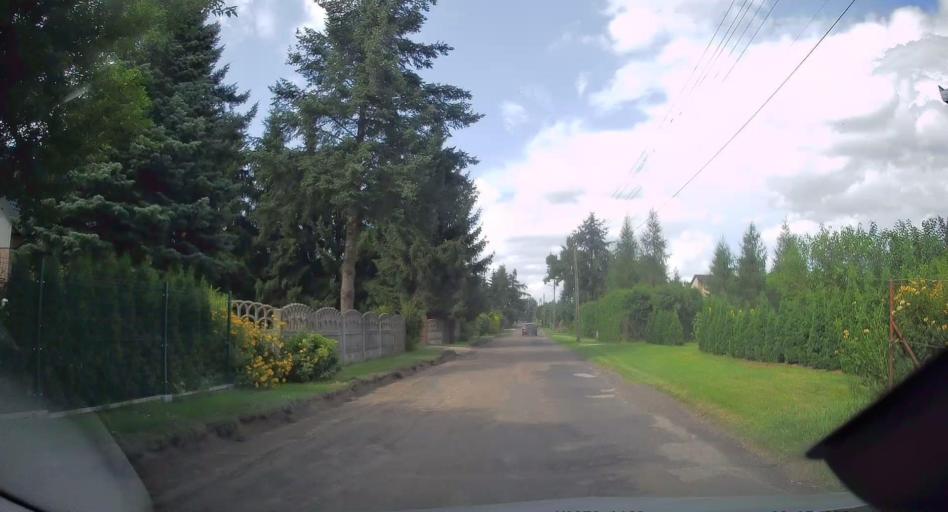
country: PL
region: Lodz Voivodeship
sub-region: Powiat brzezinski
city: Rogow
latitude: 51.8132
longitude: 19.8965
